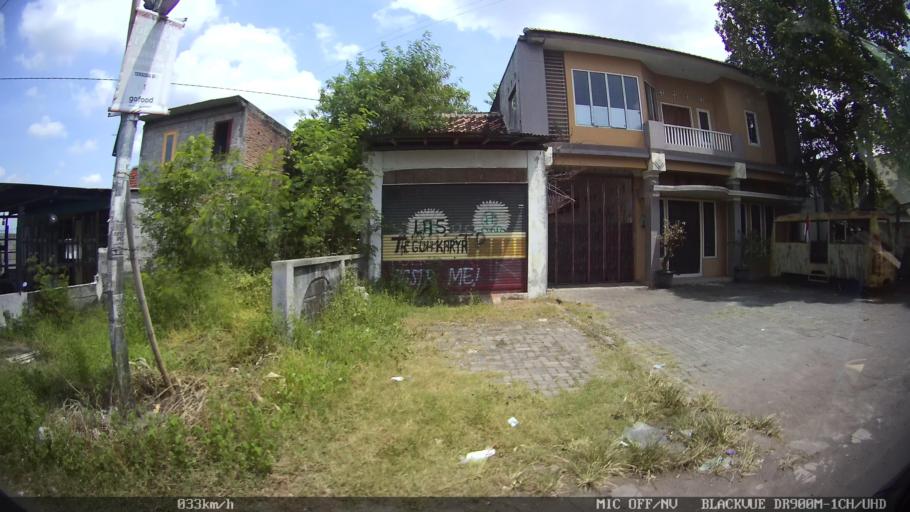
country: ID
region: Daerah Istimewa Yogyakarta
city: Kasihan
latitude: -7.8226
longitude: 110.3475
